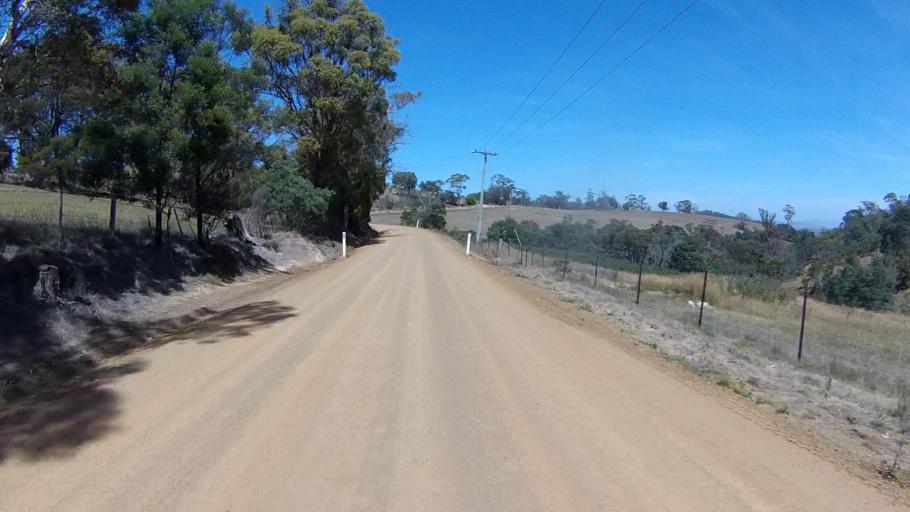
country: AU
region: Tasmania
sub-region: Sorell
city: Sorell
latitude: -42.7799
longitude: 147.6492
